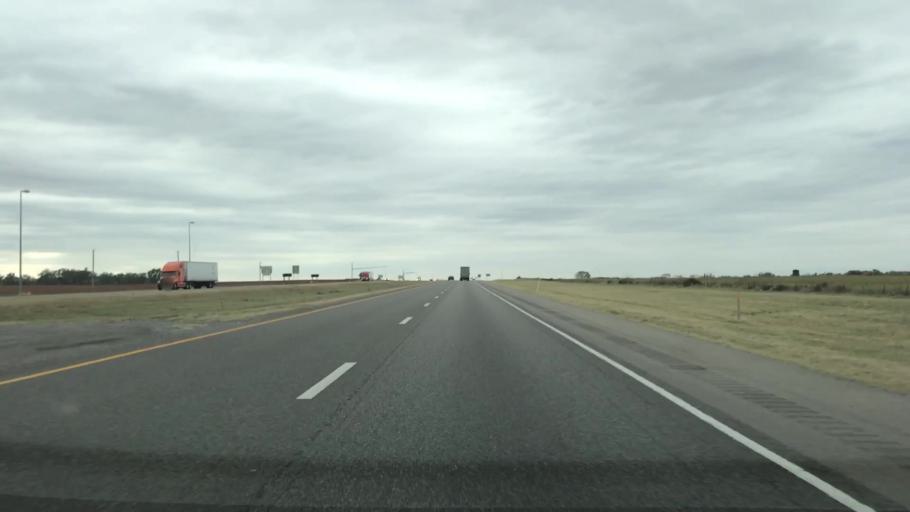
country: US
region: Oklahoma
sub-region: Beckham County
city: Erick
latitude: 35.2299
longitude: -99.9766
